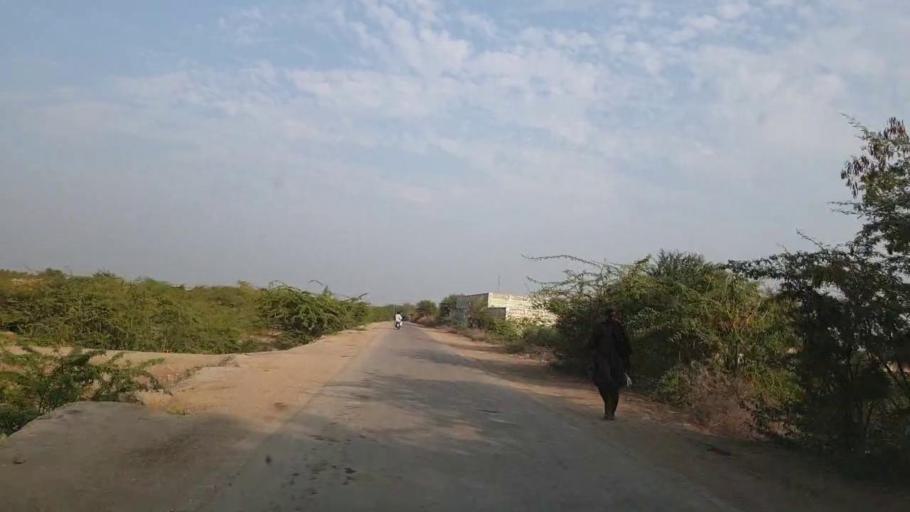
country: PK
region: Sindh
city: Pithoro
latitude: 25.5830
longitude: 69.3547
